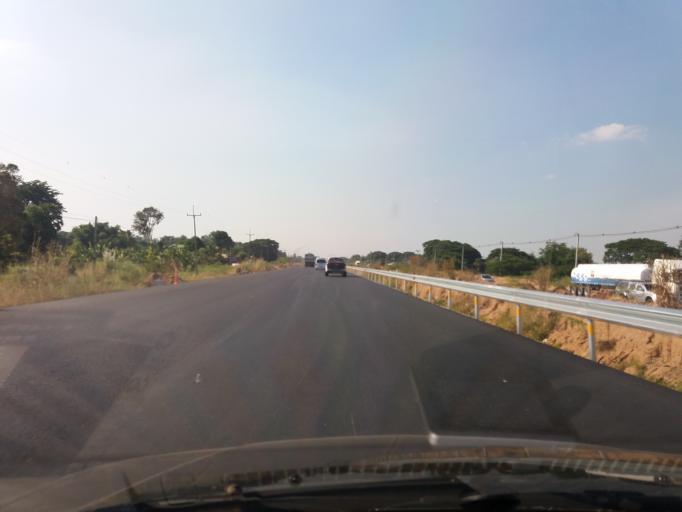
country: TH
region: Nakhon Sawan
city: Krok Phra
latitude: 15.6268
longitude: 100.1086
